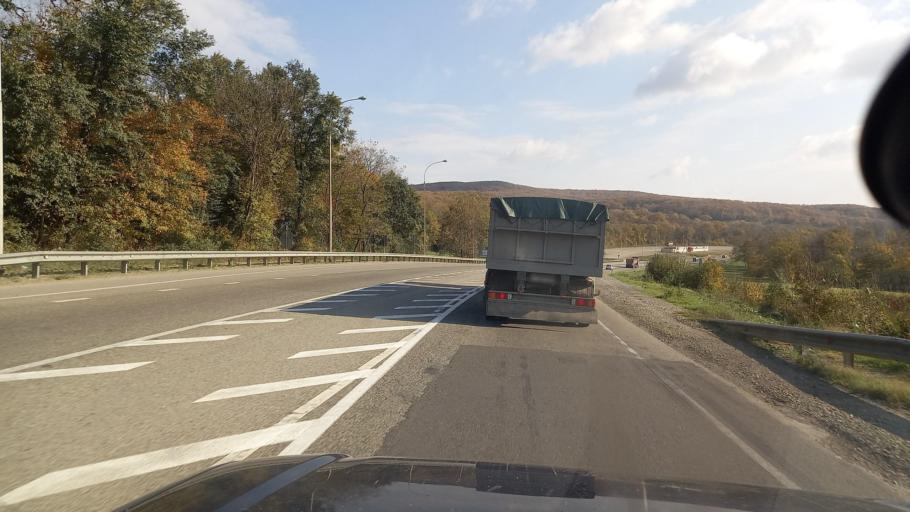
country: RU
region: Krasnodarskiy
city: Gayduk
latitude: 44.8757
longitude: 37.7758
